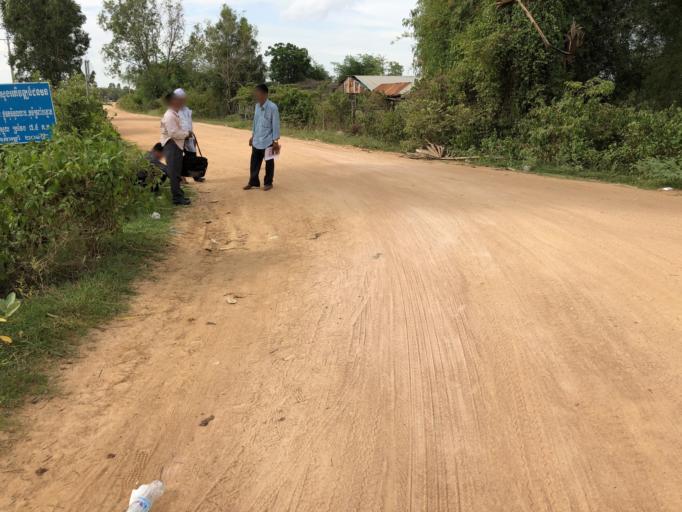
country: KH
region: Phnom Penh
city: Phnom Penh
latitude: 11.5834
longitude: 104.7294
